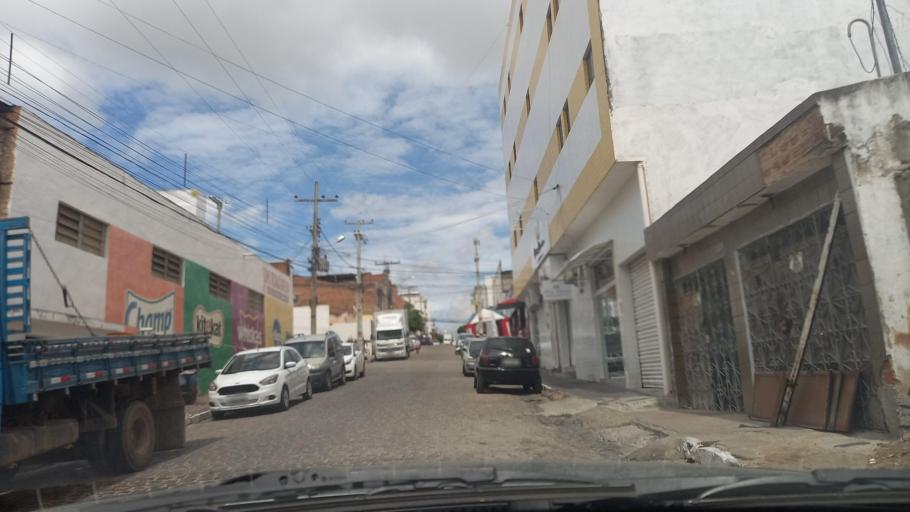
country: BR
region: Pernambuco
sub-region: Caruaru
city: Caruaru
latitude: -8.2724
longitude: -35.9593
